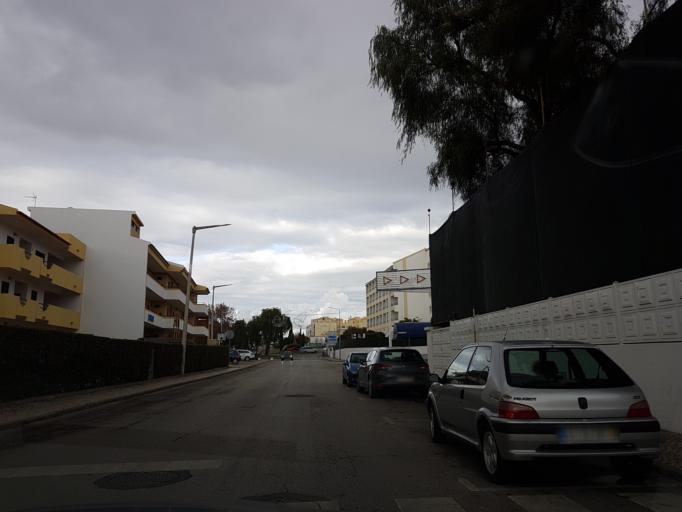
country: PT
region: Faro
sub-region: Albufeira
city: Albufeira
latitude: 37.0924
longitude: -8.2330
